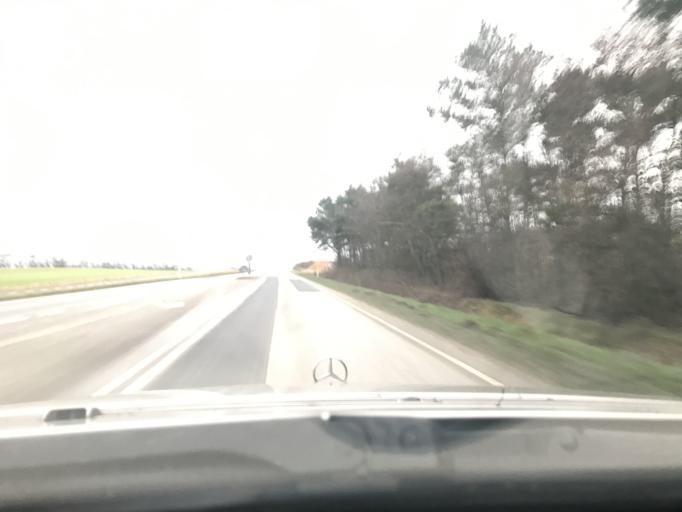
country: DK
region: South Denmark
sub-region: Tonder Kommune
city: Toftlund
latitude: 55.1412
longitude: 9.1190
